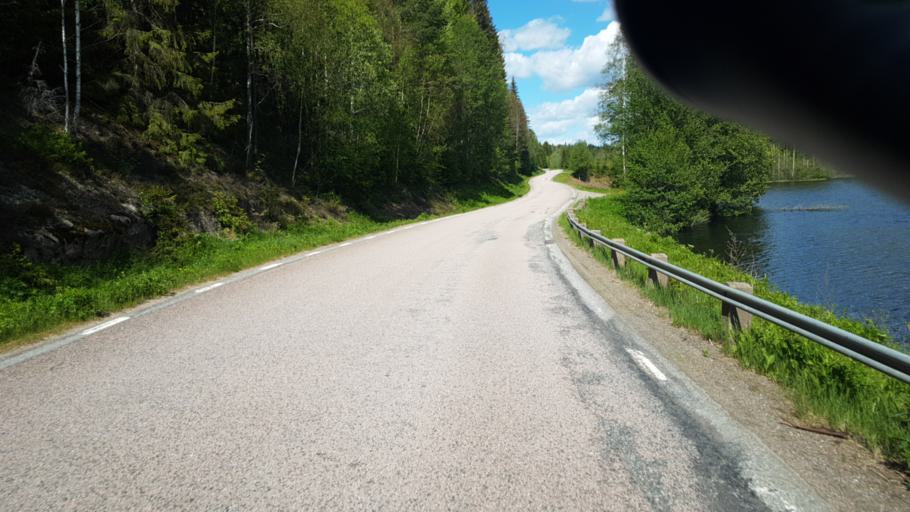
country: SE
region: Vaermland
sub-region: Arvika Kommun
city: Arvika
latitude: 59.6999
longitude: 12.7912
